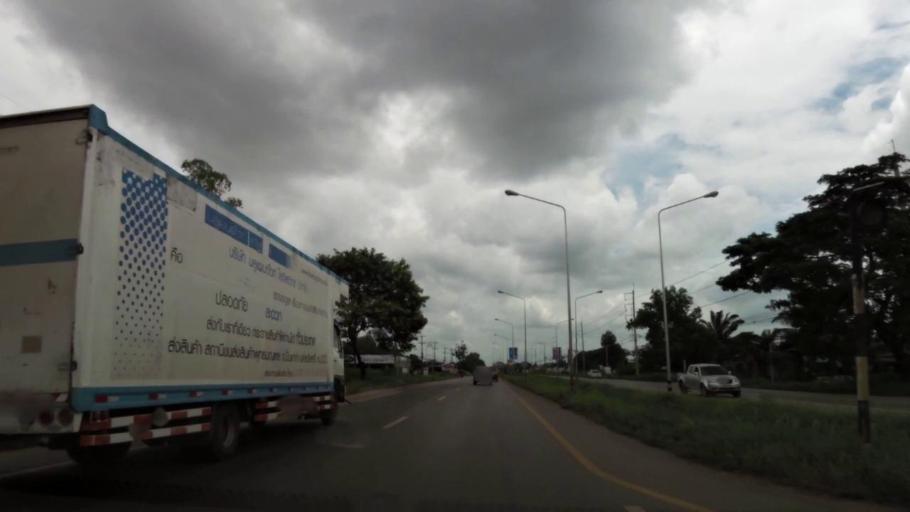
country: TH
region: Rayong
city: Klaeng
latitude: 12.7791
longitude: 101.7030
